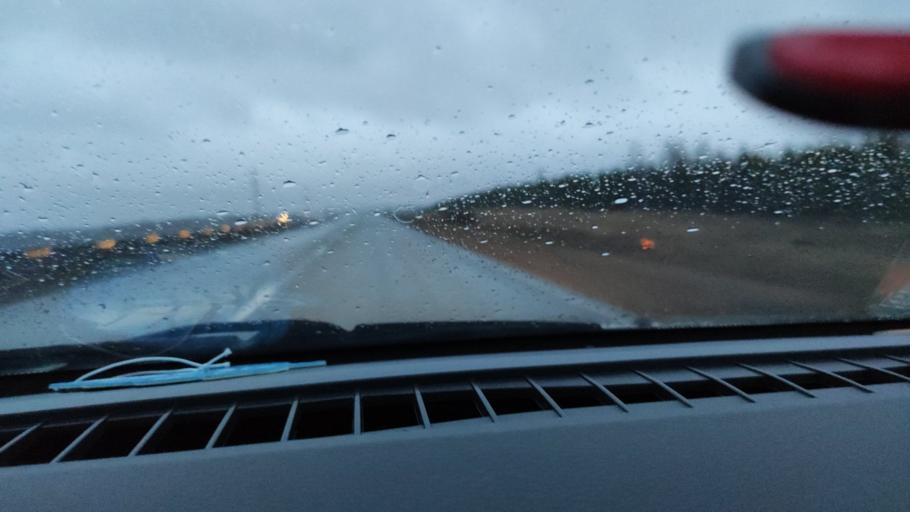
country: RU
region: Udmurtiya
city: Alnashi
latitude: 56.2762
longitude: 52.3612
